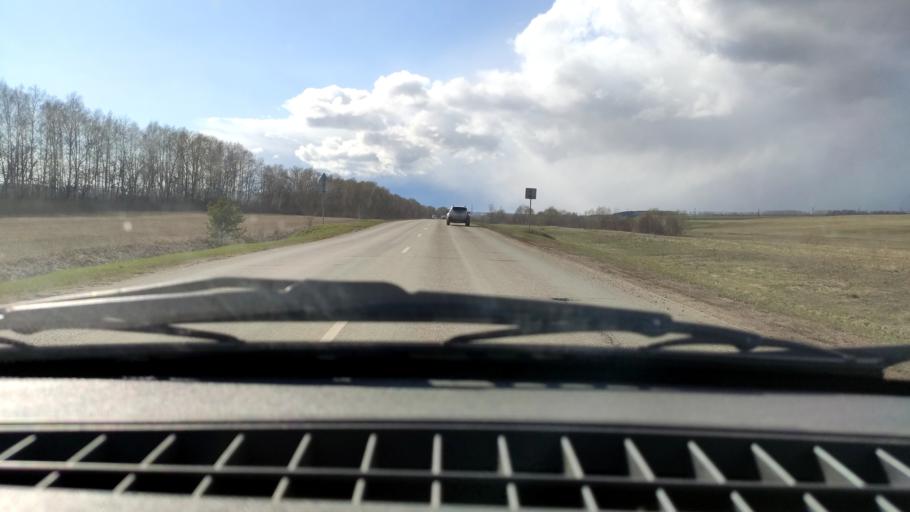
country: RU
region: Bashkortostan
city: Chekmagush
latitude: 55.1200
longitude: 54.7435
